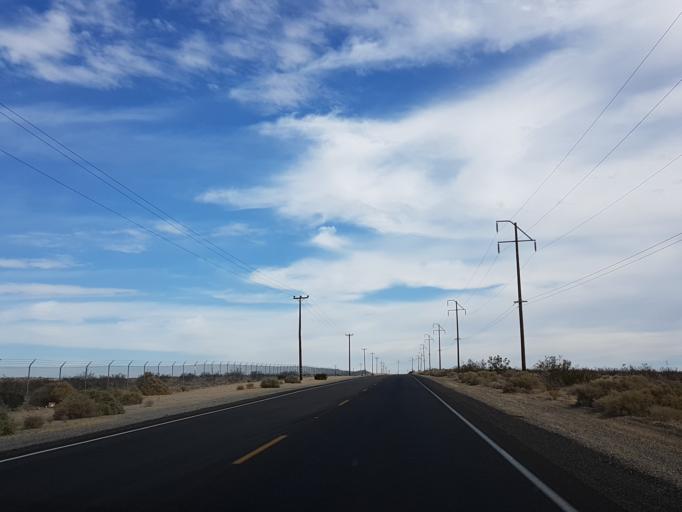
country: US
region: California
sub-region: Kern County
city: Ridgecrest
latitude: 35.6226
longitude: -117.6059
